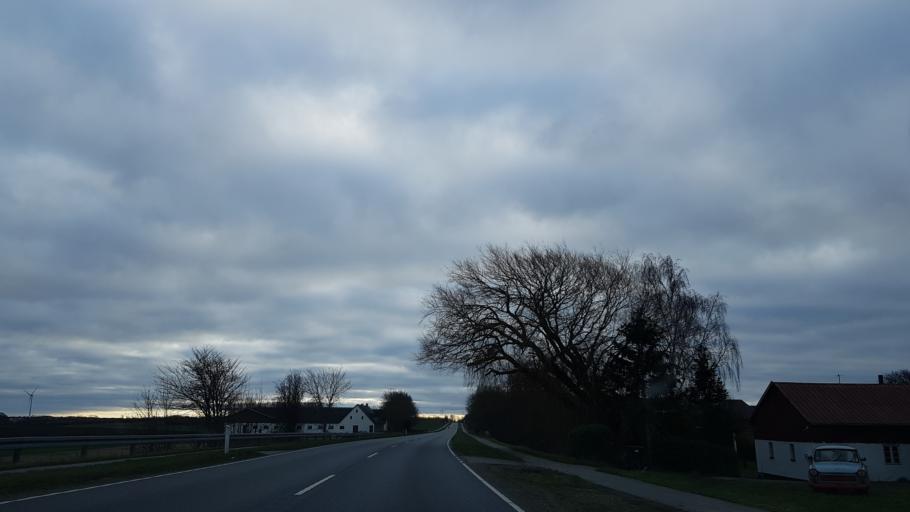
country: DK
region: Zealand
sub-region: Kalundborg Kommune
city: Gorlev
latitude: 55.5787
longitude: 11.1912
